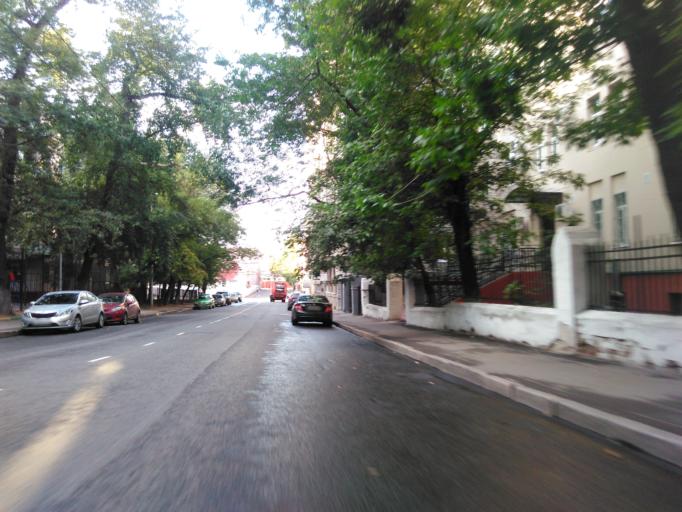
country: RU
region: Moscow
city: Sokol'niki
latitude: 55.7710
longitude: 37.6634
